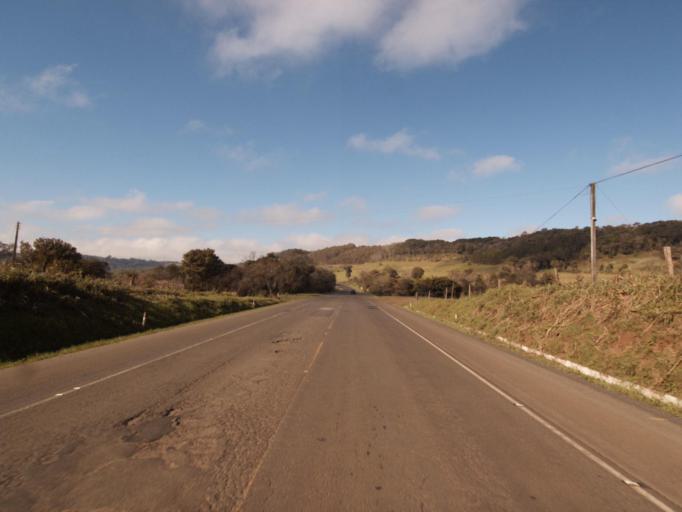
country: BR
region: Rio Grande do Sul
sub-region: Frederico Westphalen
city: Frederico Westphalen
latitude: -27.0520
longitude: -53.2291
